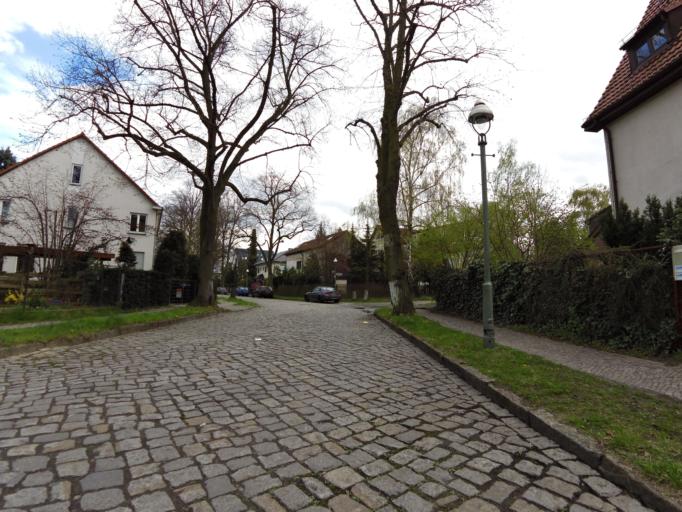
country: DE
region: Berlin
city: Lichtenrade
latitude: 52.3830
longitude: 13.4009
